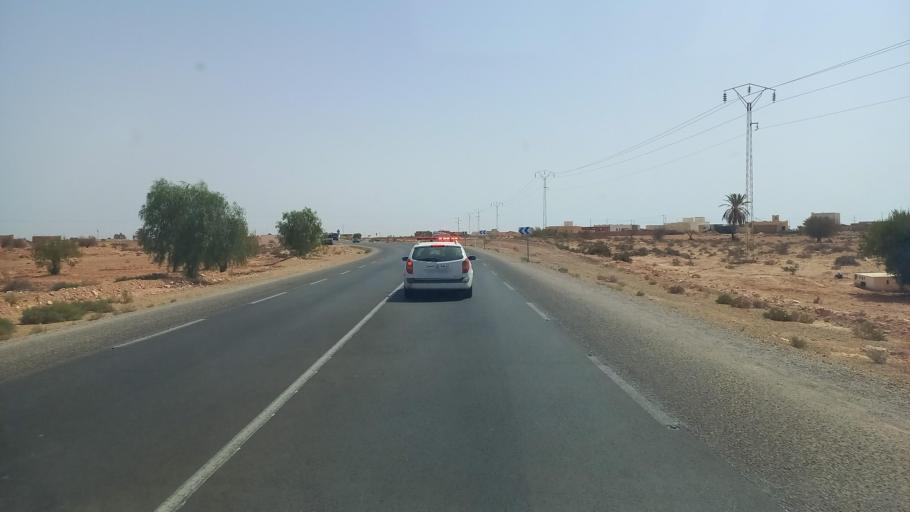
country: TN
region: Madanin
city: Medenine
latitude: 33.3696
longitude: 10.6844
